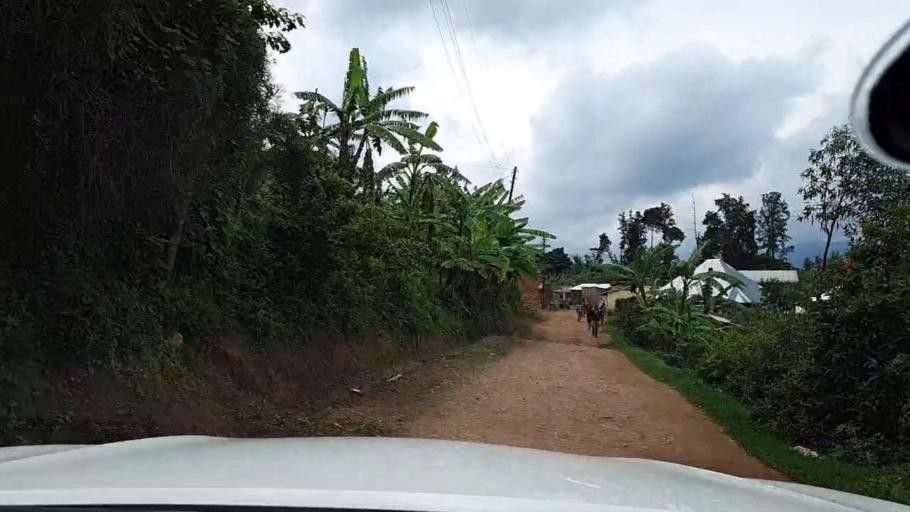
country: RW
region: Western Province
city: Kibuye
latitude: -2.1860
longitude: 29.2935
